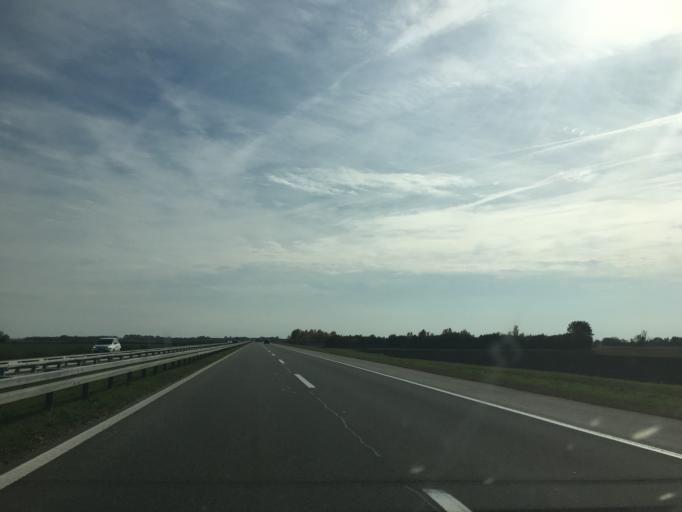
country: RS
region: Autonomna Pokrajina Vojvodina
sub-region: Sremski Okrug
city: Stara Pazova
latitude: 45.0250
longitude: 20.1909
